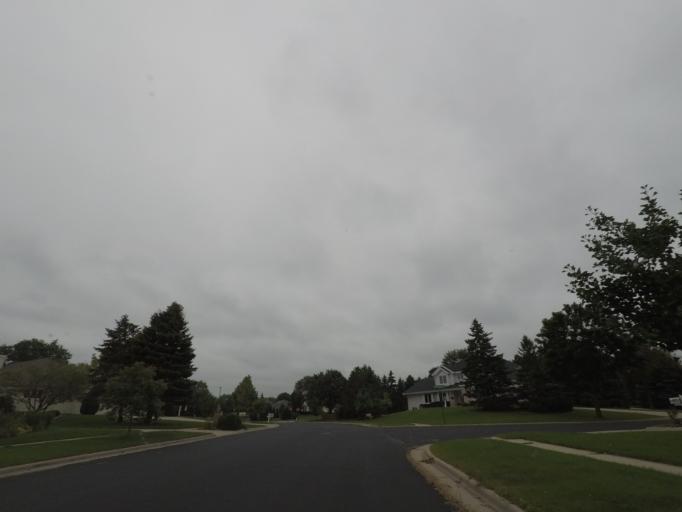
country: US
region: Wisconsin
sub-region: Dane County
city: Middleton
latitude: 43.0850
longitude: -89.4992
